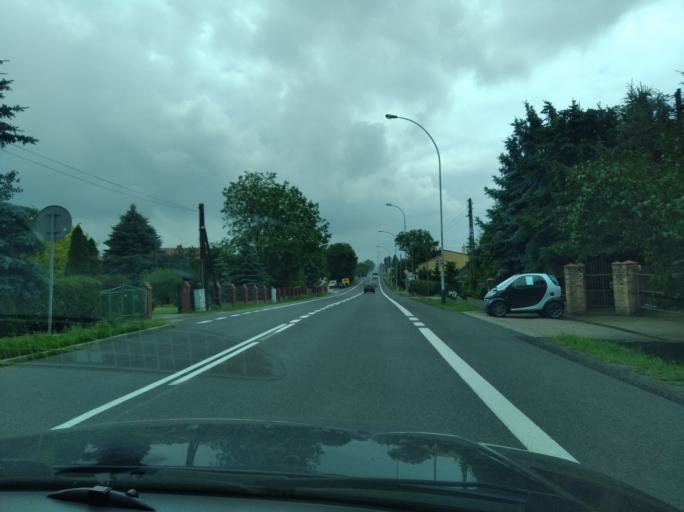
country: PL
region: Subcarpathian Voivodeship
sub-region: Powiat przeworski
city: Przeworsk
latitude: 50.0575
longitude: 22.5015
